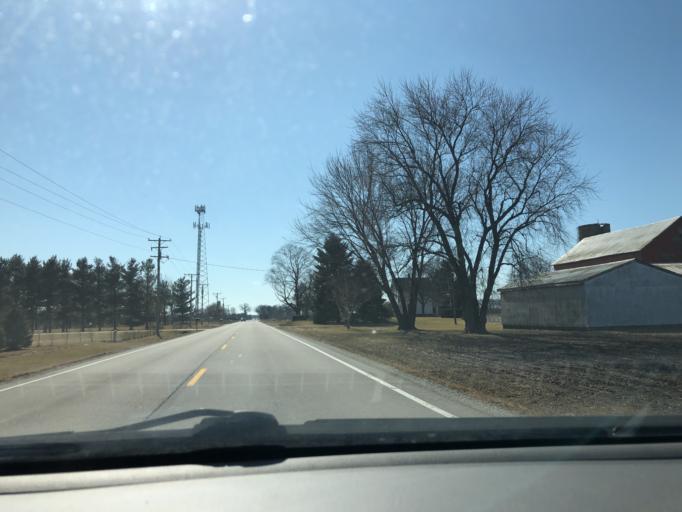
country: US
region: Illinois
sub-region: Kane County
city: Hampshire
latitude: 42.1239
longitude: -88.5350
